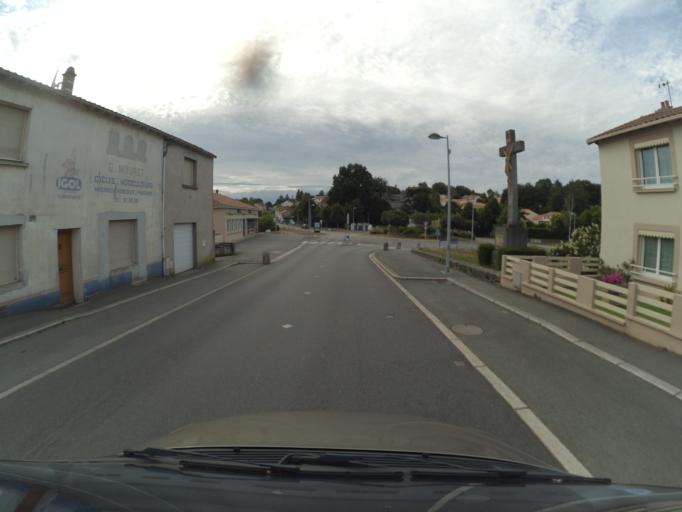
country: FR
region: Pays de la Loire
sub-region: Departement de la Vendee
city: Mortagne-sur-Sevre
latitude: 46.9945
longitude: -0.9523
